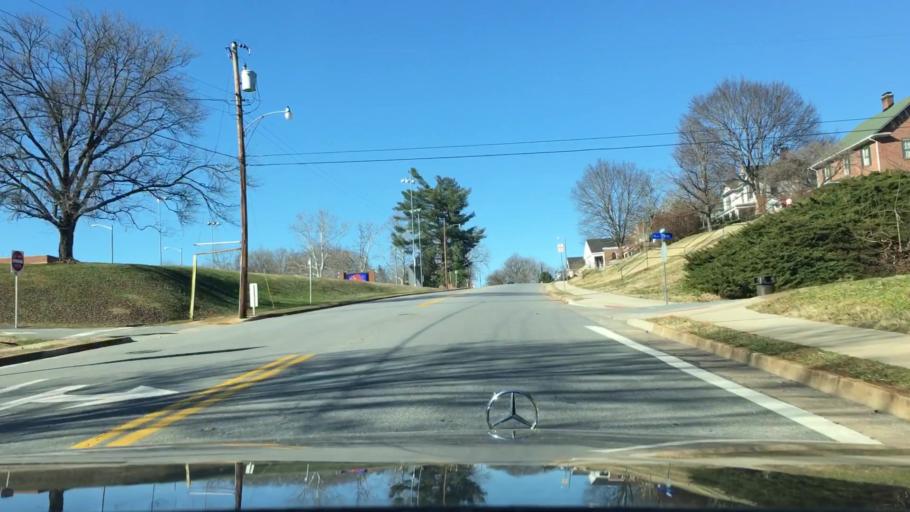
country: US
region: Virginia
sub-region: Campbell County
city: Altavista
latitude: 37.1096
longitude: -79.2938
